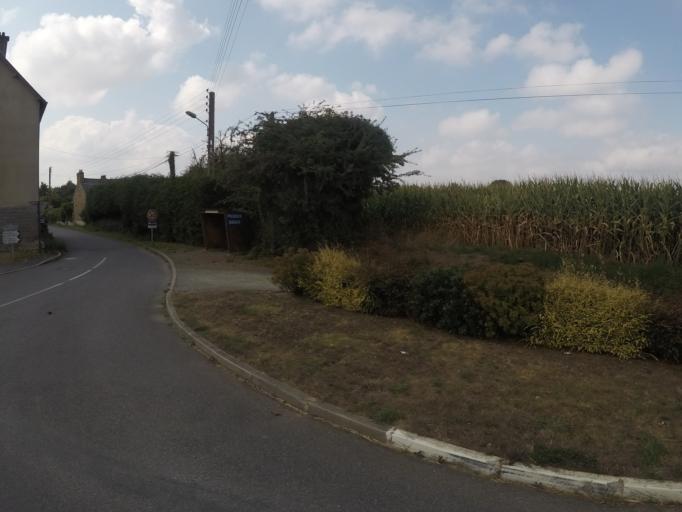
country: FR
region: Brittany
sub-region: Departement des Cotes-d'Armor
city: Plelo
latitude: 48.5469
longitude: -2.9644
